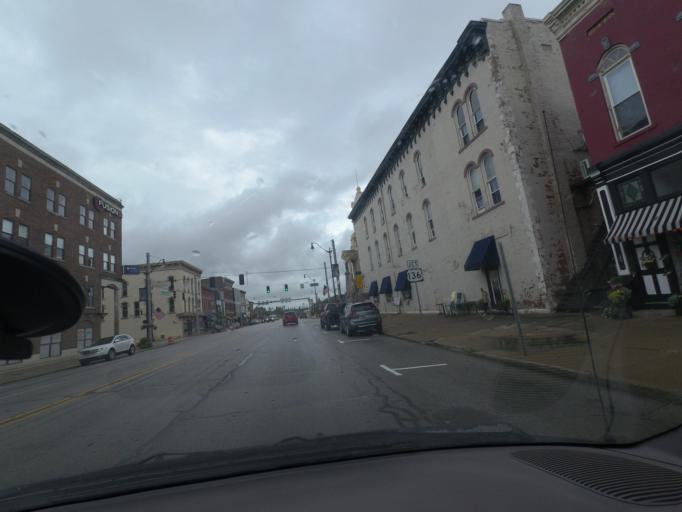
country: US
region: Indiana
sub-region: Montgomery County
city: Crawfordsville
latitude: 40.0412
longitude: -86.9013
